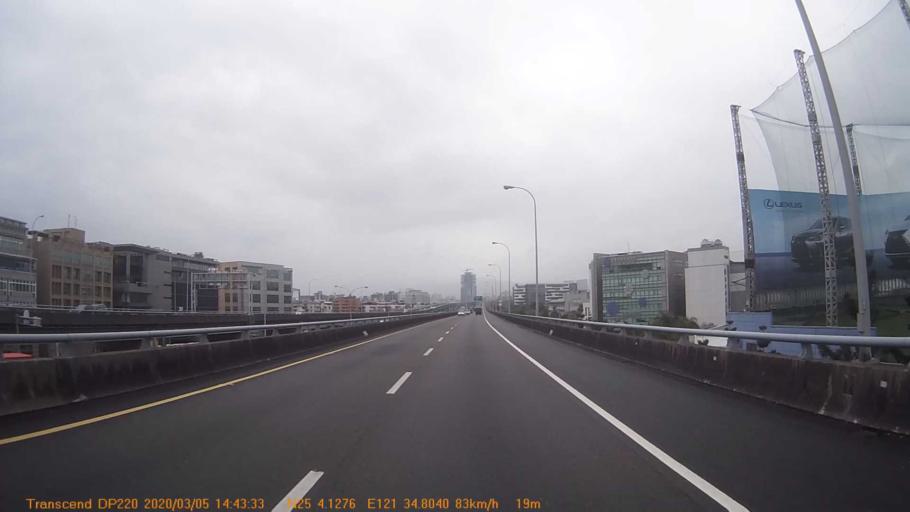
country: TW
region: Taipei
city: Taipei
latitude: 25.0685
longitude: 121.5795
